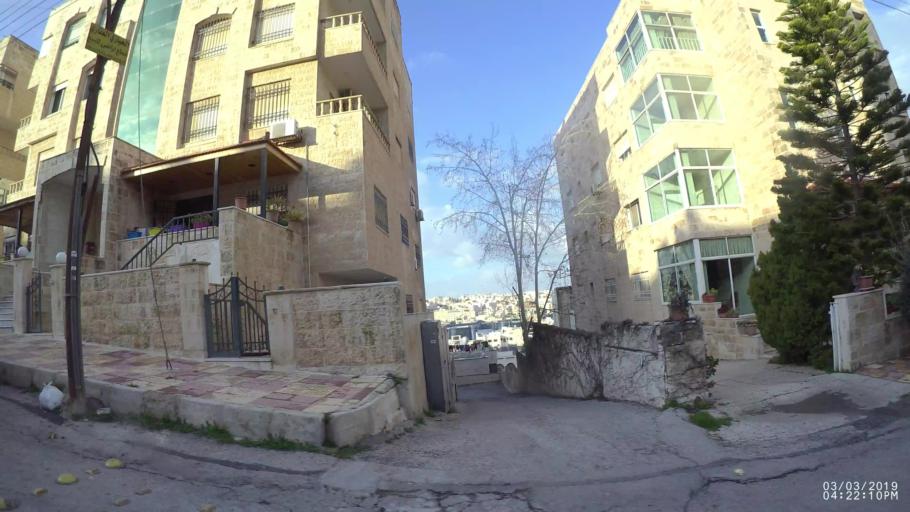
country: JO
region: Amman
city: Al Jubayhah
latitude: 31.9819
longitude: 35.8861
